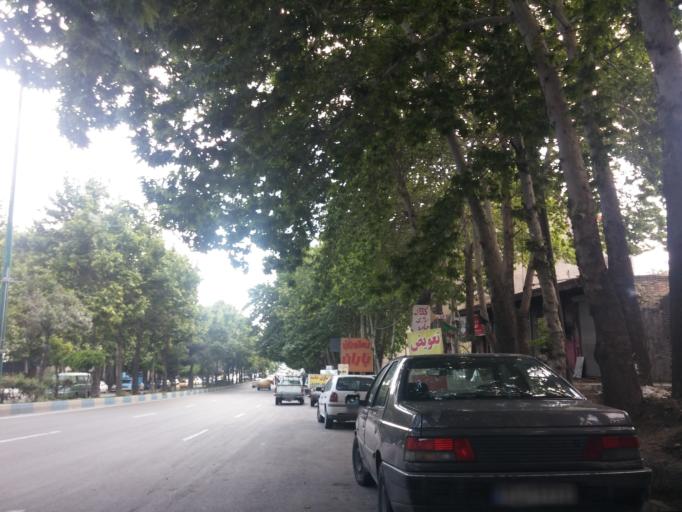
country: IR
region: Tehran
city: Damavand
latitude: 35.7378
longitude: 51.9188
